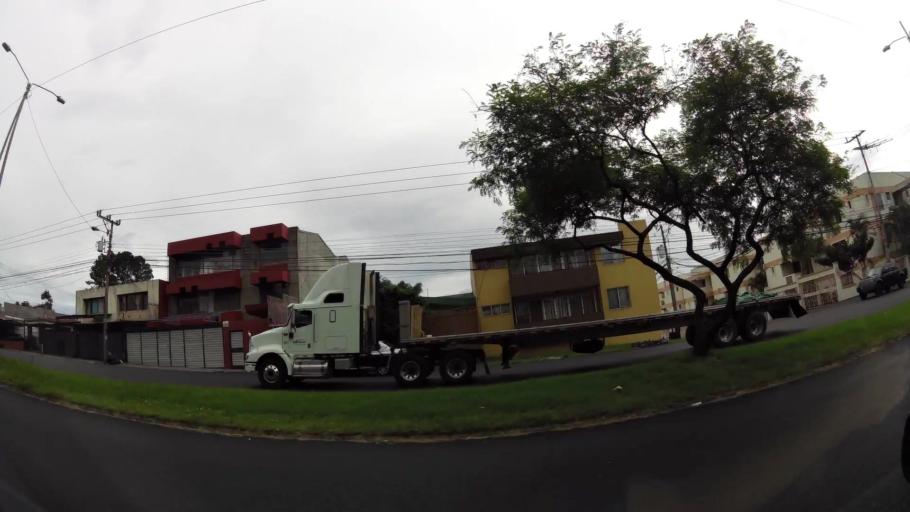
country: CR
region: San Jose
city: San Pedro
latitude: 9.9287
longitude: -84.0550
